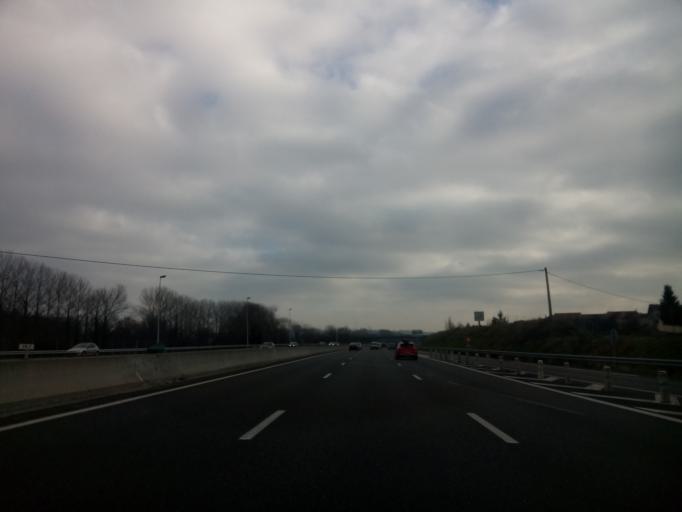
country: FR
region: Rhone-Alpes
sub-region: Departement de l'Isere
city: Saint-Alban-de-Roche
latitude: 45.6123
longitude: 5.2154
